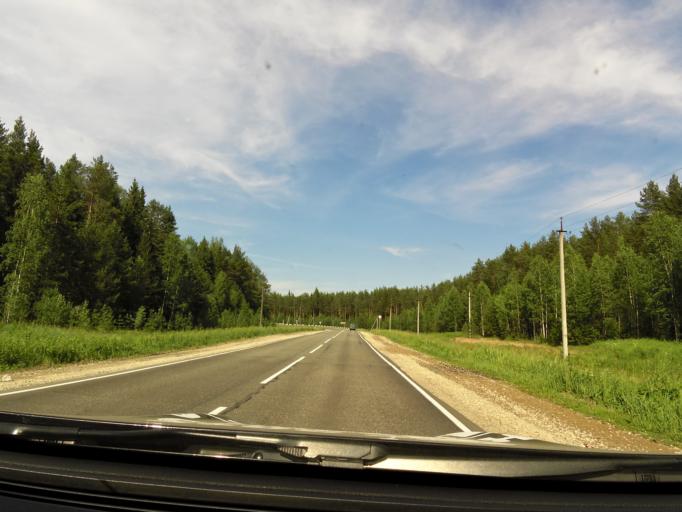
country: RU
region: Kirov
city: Belaya Kholunitsa
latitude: 58.8327
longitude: 50.6872
